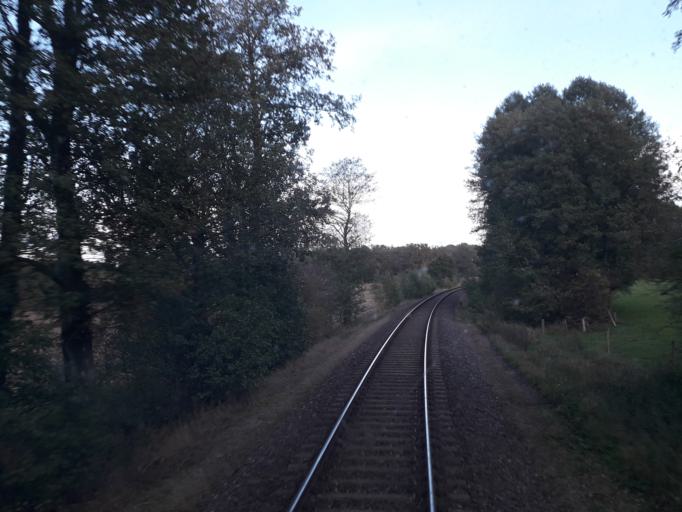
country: DE
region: Brandenburg
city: Heiligengrabe
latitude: 53.1522
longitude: 12.3528
